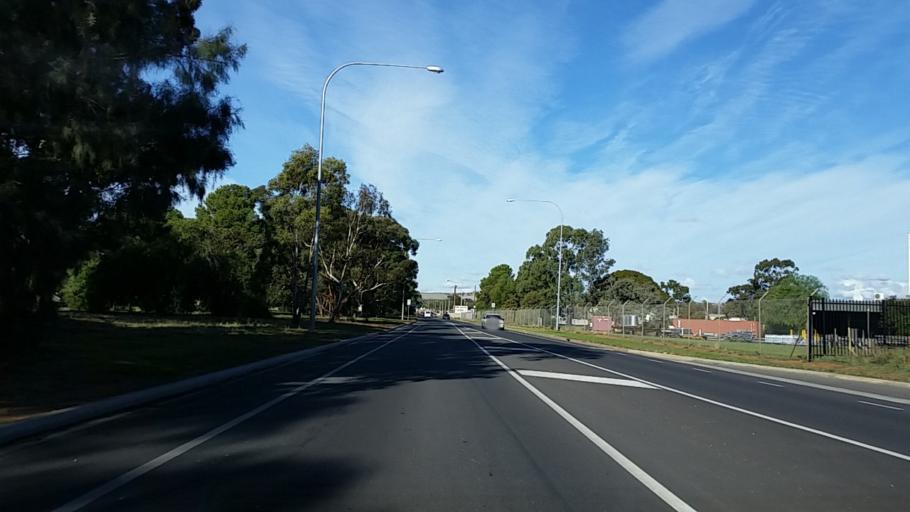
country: AU
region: South Australia
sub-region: Salisbury
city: Elizabeth
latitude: -34.6985
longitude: 138.6584
